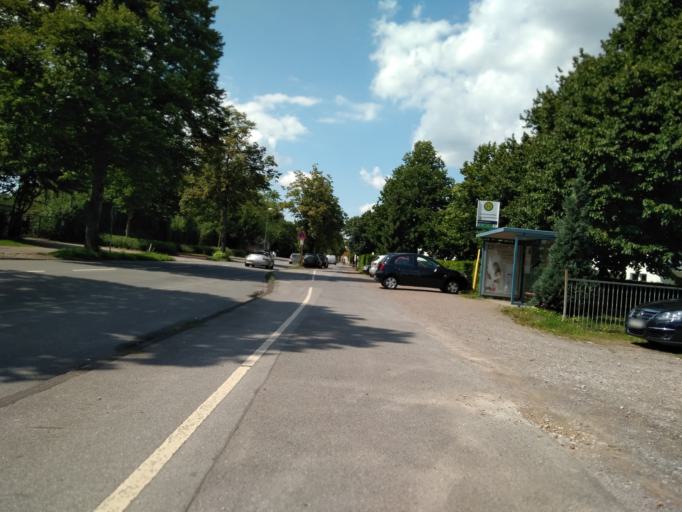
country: DE
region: North Rhine-Westphalia
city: Dorsten
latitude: 51.6586
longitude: 6.9780
